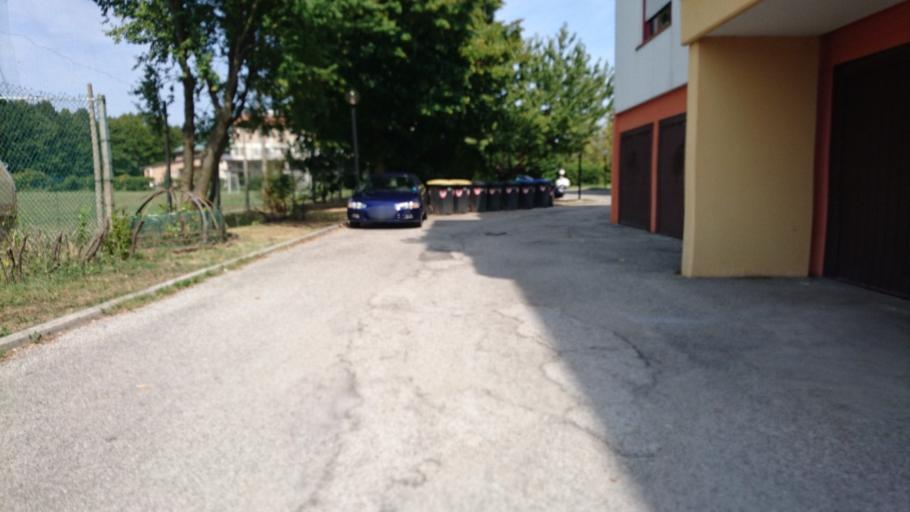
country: IT
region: Veneto
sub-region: Provincia di Padova
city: Albignasego
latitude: 45.3766
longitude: 11.8896
